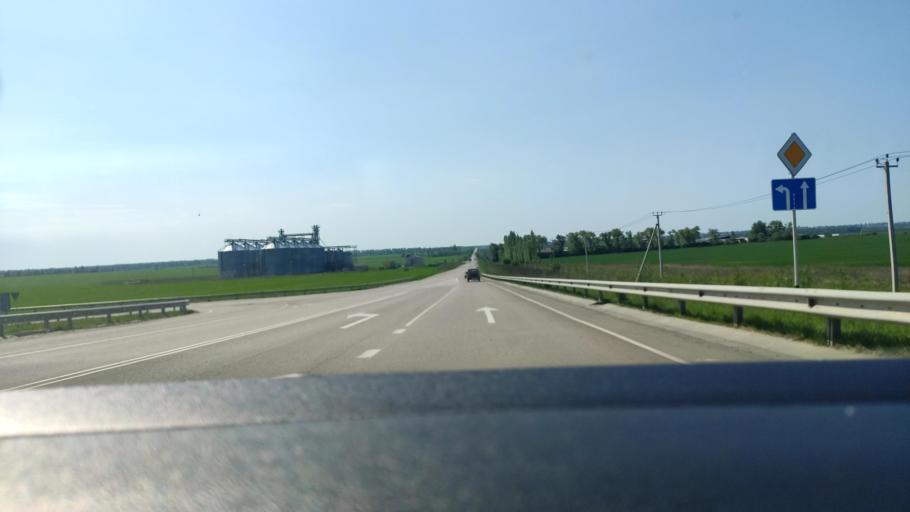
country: RU
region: Voronezj
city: Novaya Usman'
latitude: 51.5873
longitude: 39.3742
